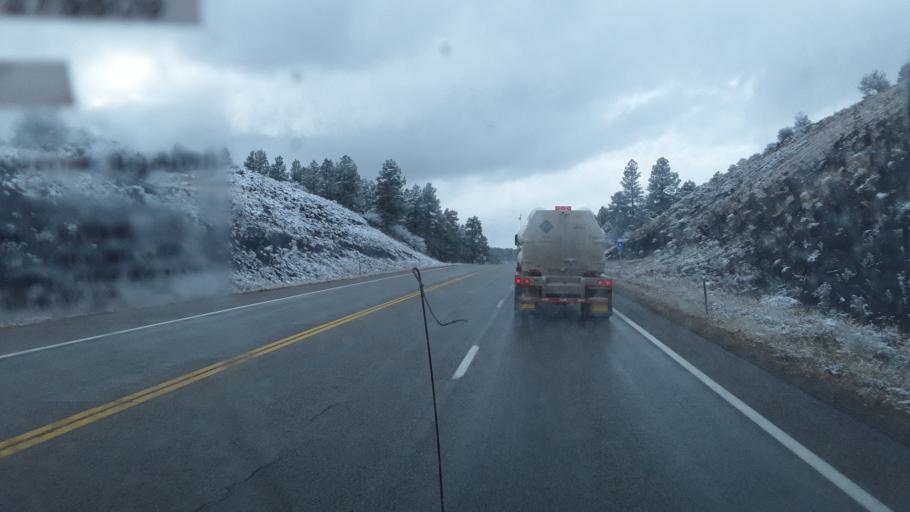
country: US
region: Colorado
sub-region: Archuleta County
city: Pagosa Springs
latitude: 37.2094
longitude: -107.2573
